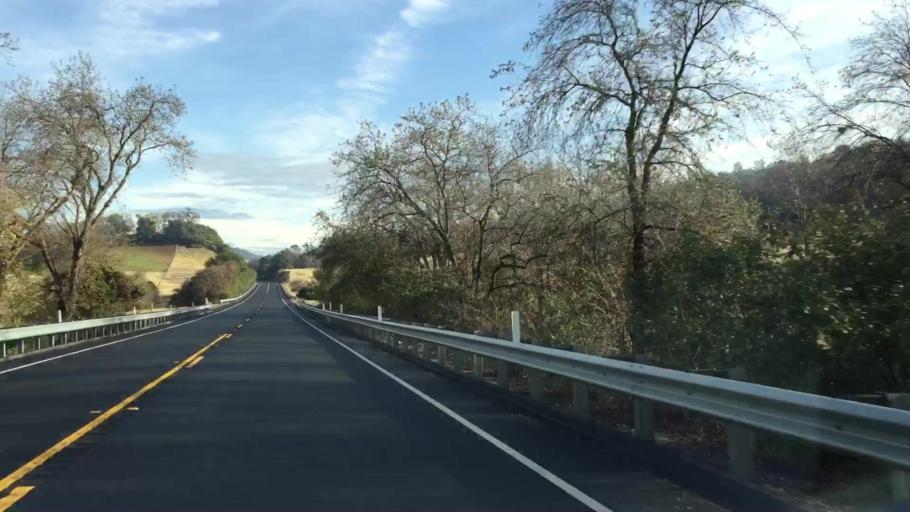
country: US
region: California
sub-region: Butte County
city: Oroville
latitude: 39.6371
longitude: -121.5787
